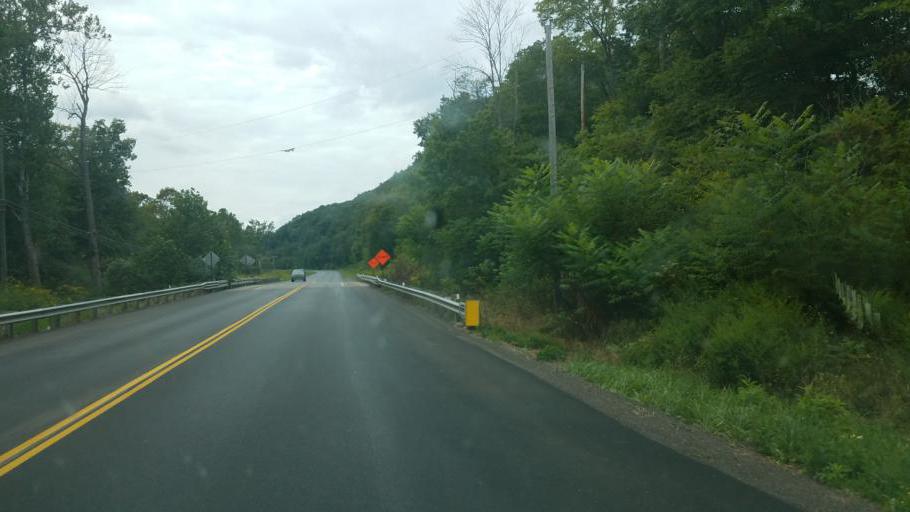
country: US
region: Ohio
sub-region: Columbiana County
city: Lisbon
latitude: 40.7658
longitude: -80.7154
